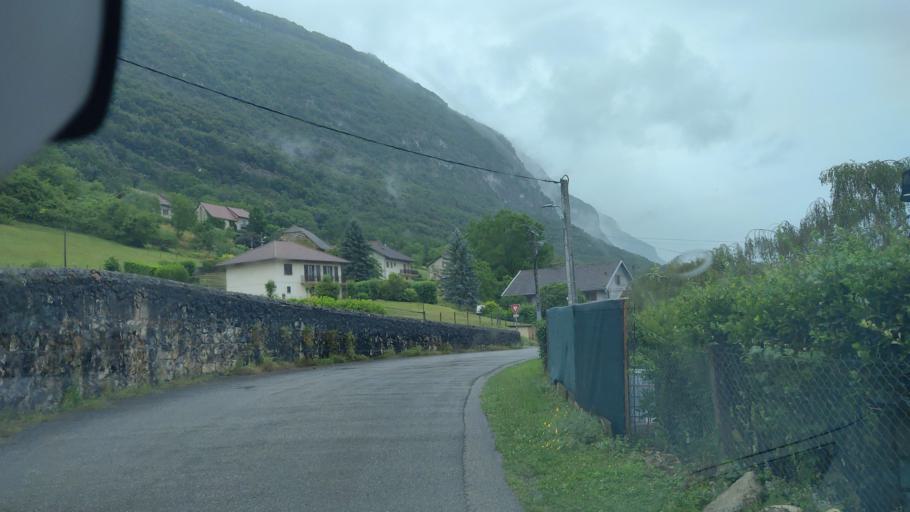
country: FR
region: Rhone-Alpes
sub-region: Departement de la Savoie
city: Chindrieux
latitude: 45.8213
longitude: 5.8524
